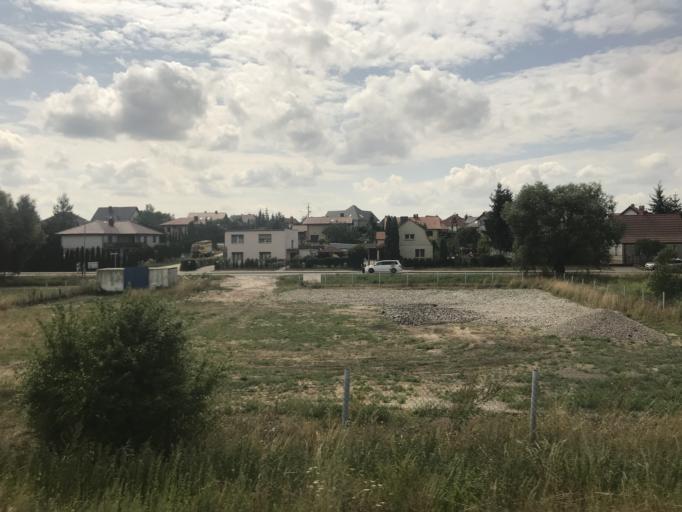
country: PL
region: Greater Poland Voivodeship
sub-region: Powiat poznanski
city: Pobiedziska
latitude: 52.4753
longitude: 17.2488
